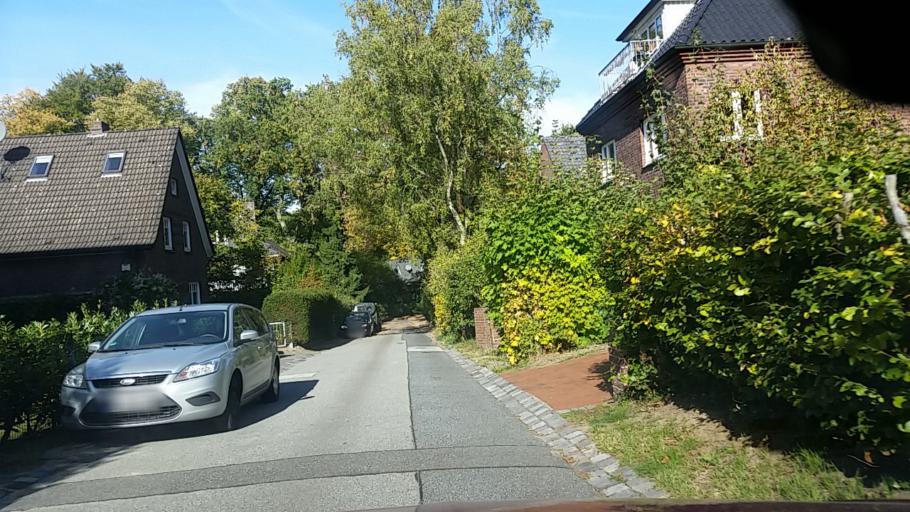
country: DE
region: Schleswig-Holstein
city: Halstenbek
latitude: 53.5690
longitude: 9.8055
